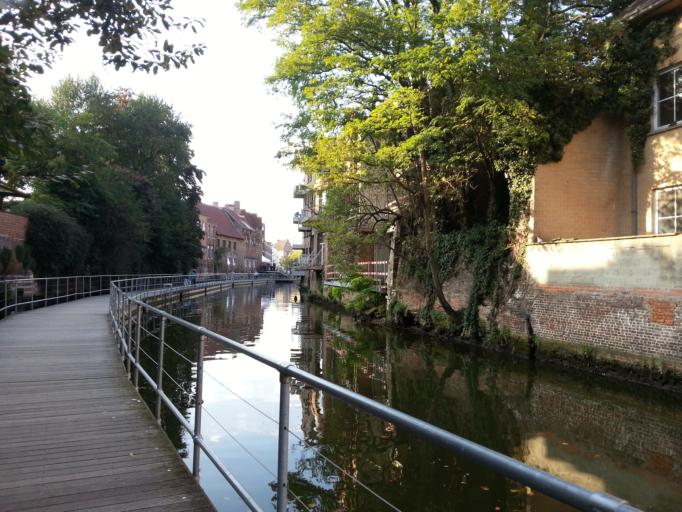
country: BE
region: Flanders
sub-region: Provincie Antwerpen
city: Mechelen
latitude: 51.0232
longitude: 4.4807
